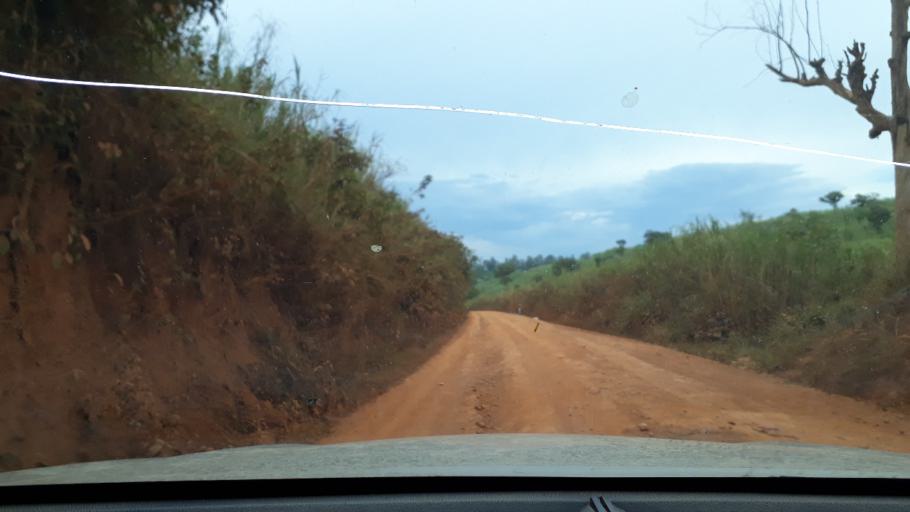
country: CD
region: Eastern Province
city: Bunia
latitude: 1.8349
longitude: 30.4570
